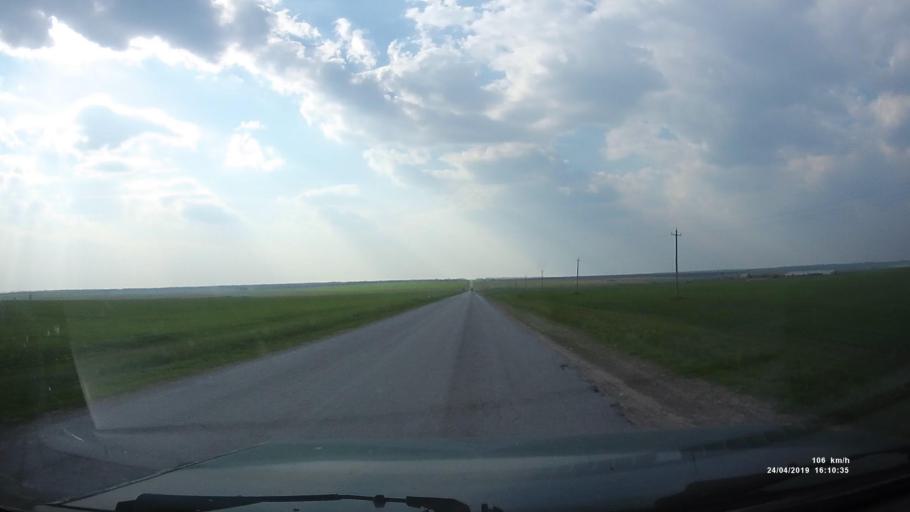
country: RU
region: Rostov
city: Sovetskoye
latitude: 46.7183
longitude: 42.2679
